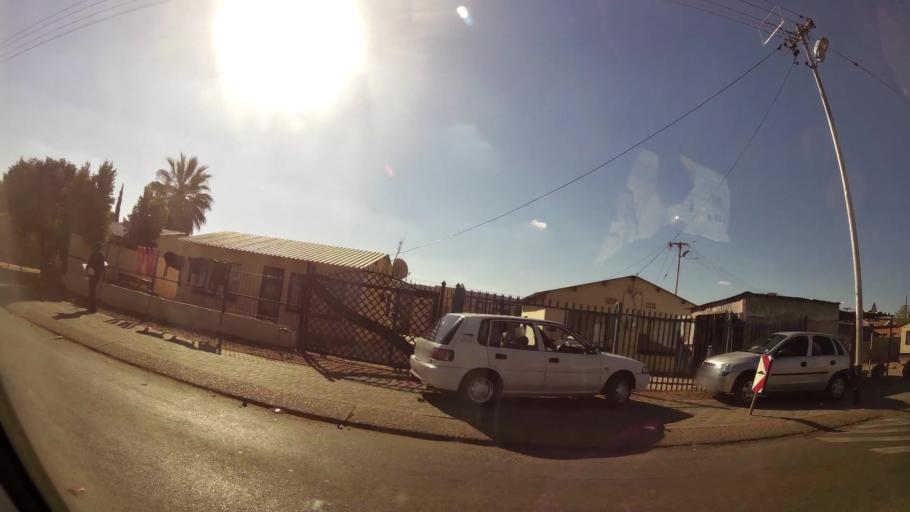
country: ZA
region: Gauteng
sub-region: City of Tshwane Metropolitan Municipality
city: Cullinan
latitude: -25.7122
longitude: 28.3859
